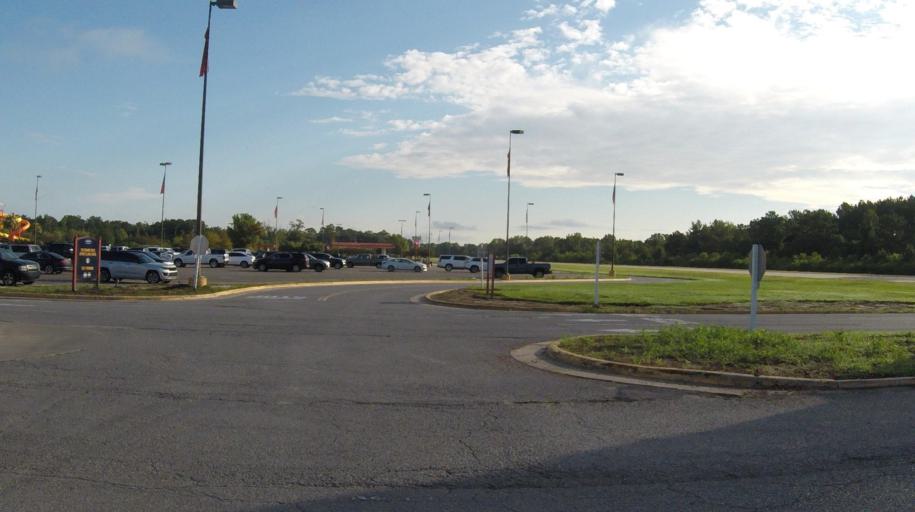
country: US
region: Louisiana
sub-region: Allen Parish
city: Kinder
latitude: 30.5448
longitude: -92.8123
